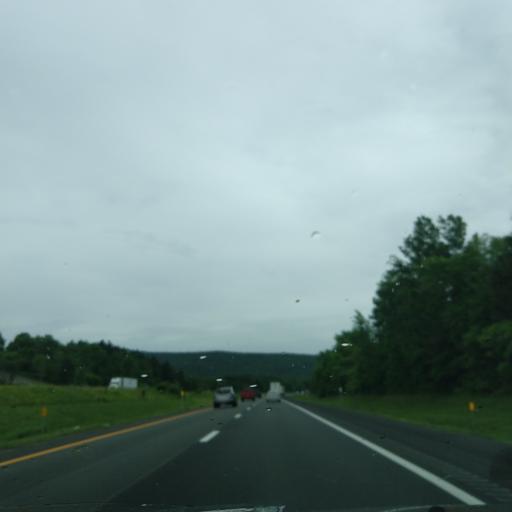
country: US
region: New York
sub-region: Broome County
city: Chenango Bridge
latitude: 42.0791
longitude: -75.8044
